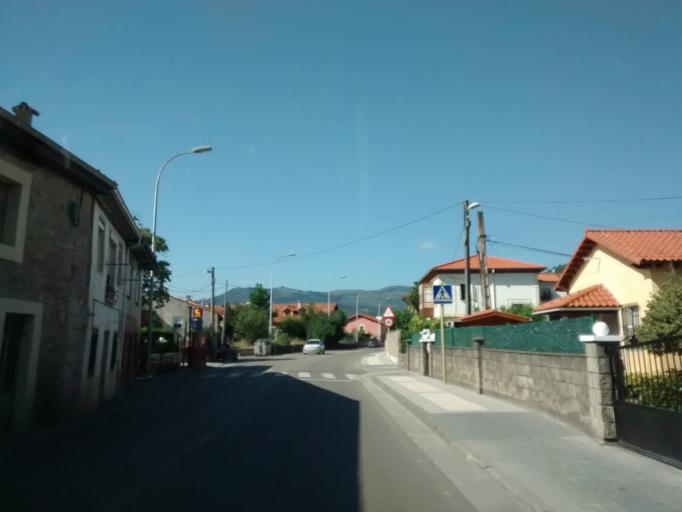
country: ES
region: Cantabria
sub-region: Provincia de Cantabria
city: Cartes
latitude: 43.3371
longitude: -4.0605
